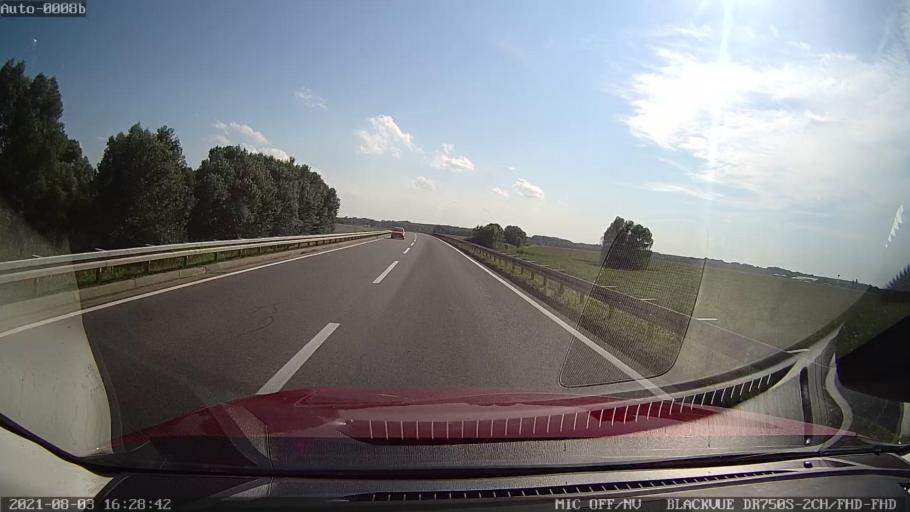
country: HR
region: Osjecko-Baranjska
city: Darda
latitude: 45.6063
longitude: 18.6626
